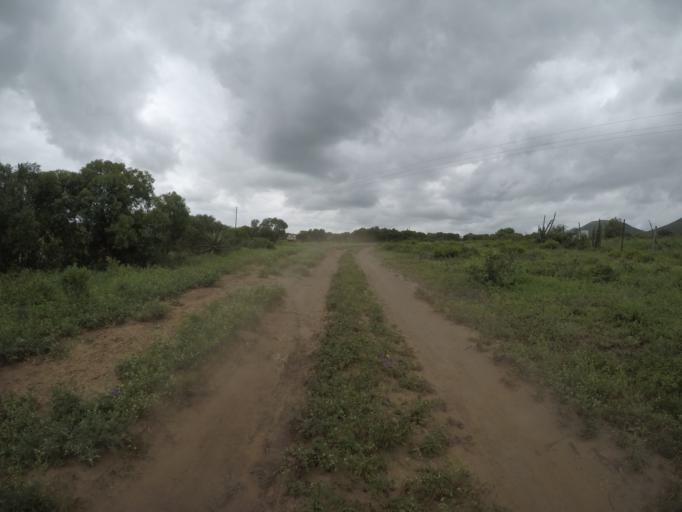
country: ZA
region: KwaZulu-Natal
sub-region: uThungulu District Municipality
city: Empangeni
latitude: -28.5832
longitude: 31.8618
